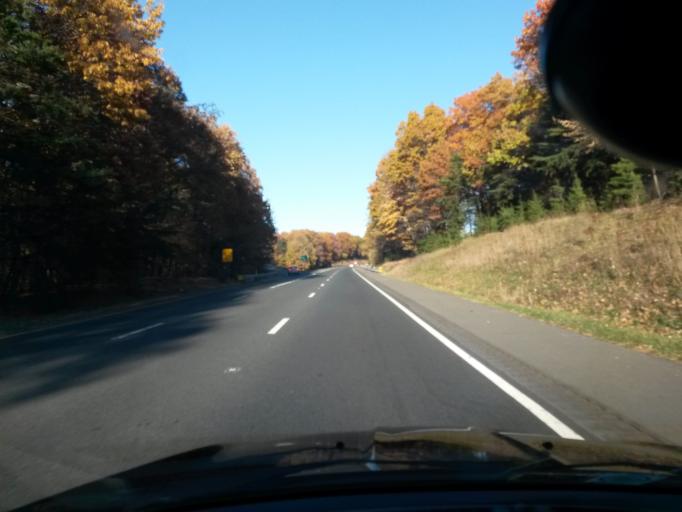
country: US
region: Virginia
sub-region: City of Lynchburg
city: West Lynchburg
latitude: 37.3594
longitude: -79.1667
